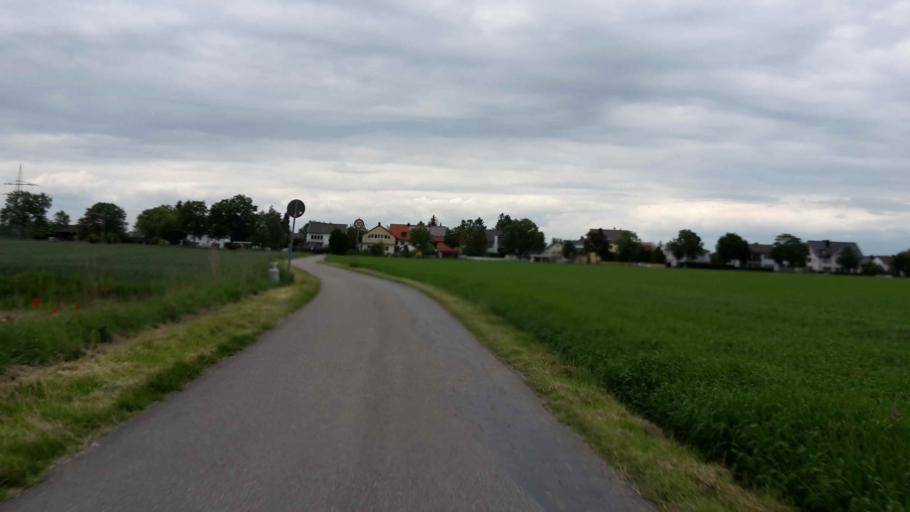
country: DE
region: Bavaria
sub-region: Upper Bavaria
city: Pasing
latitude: 48.1775
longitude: 11.4187
